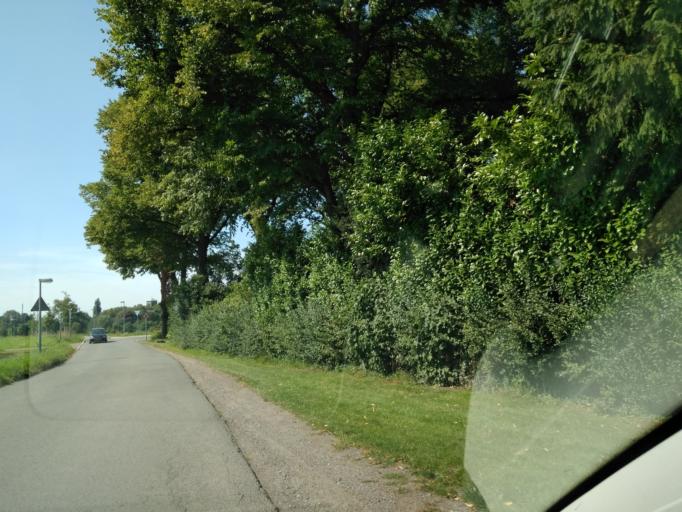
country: DE
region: North Rhine-Westphalia
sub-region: Regierungsbezirk Munster
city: Gladbeck
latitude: 51.5546
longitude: 7.0518
